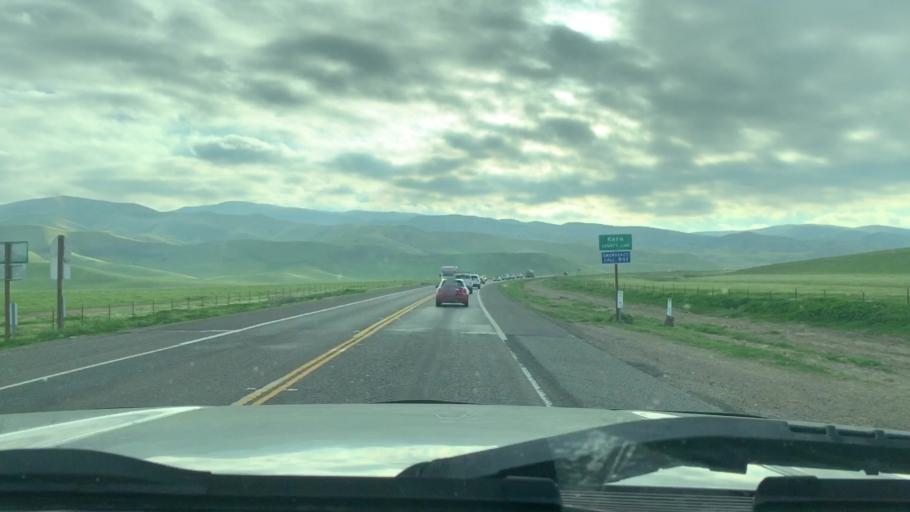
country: US
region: California
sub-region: Kings County
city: Avenal
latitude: 35.7888
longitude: -120.1128
